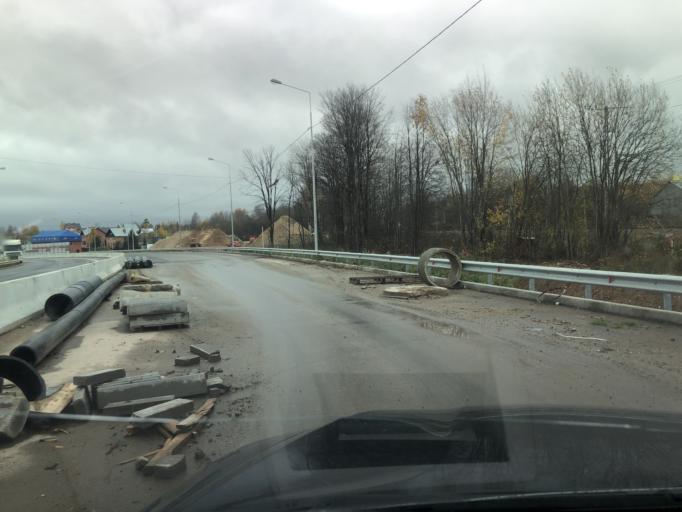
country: RU
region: Moskovskaya
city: Sergiyev Posad
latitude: 56.3432
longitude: 38.1244
